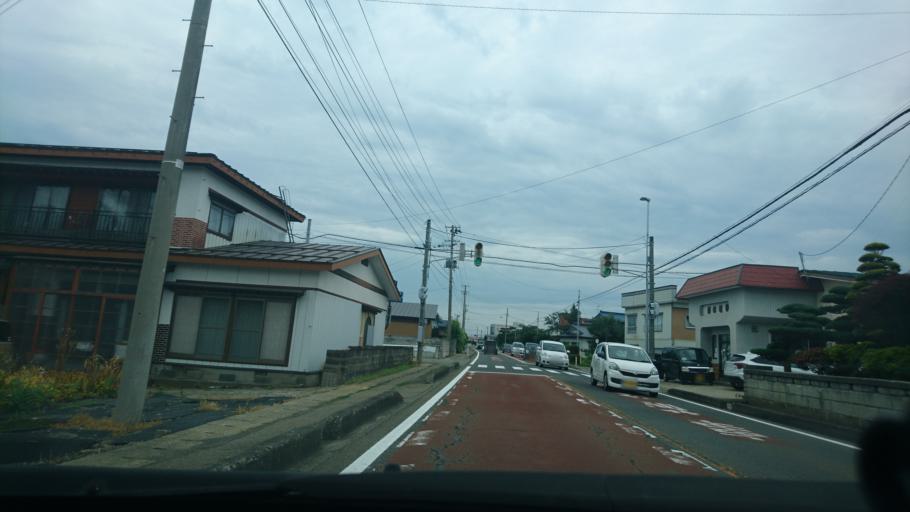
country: JP
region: Akita
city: Yokotemachi
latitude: 39.3996
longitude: 140.5633
